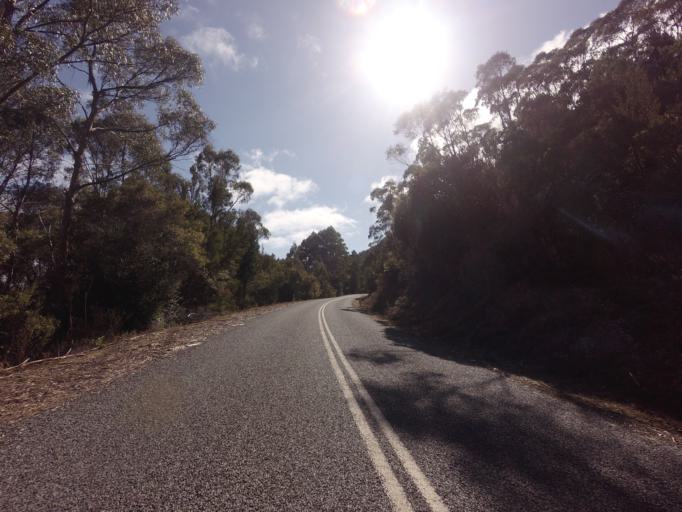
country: AU
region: Tasmania
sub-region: Huon Valley
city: Geeveston
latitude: -42.8079
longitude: 146.3923
